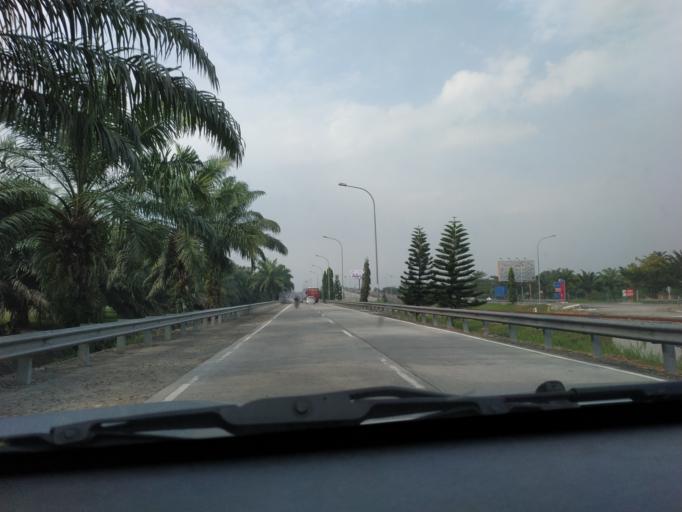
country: ID
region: North Sumatra
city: Percut
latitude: 3.6131
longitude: 98.8570
